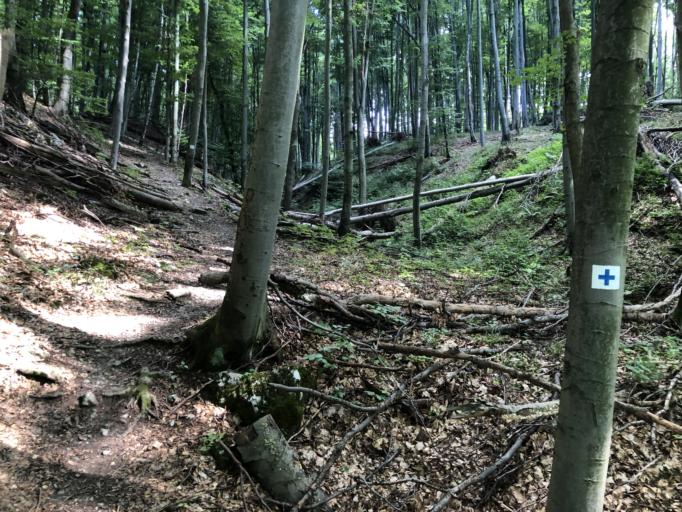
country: HU
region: Heves
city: Szilvasvarad
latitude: 48.1299
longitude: 20.5210
